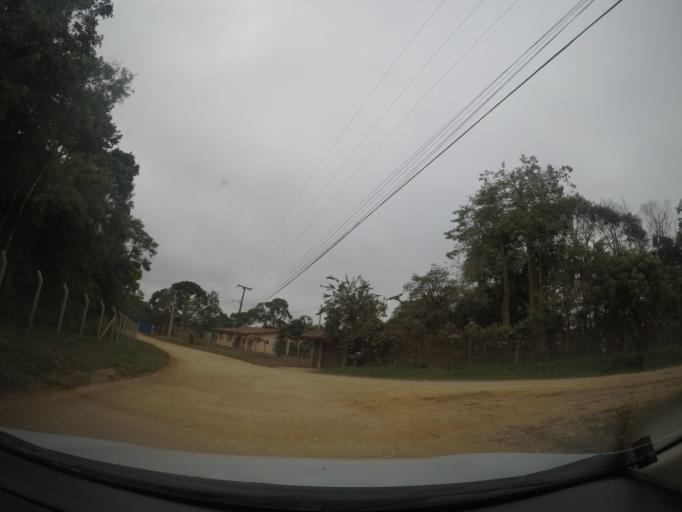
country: BR
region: Parana
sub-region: Colombo
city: Colombo
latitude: -25.3269
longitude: -49.2531
